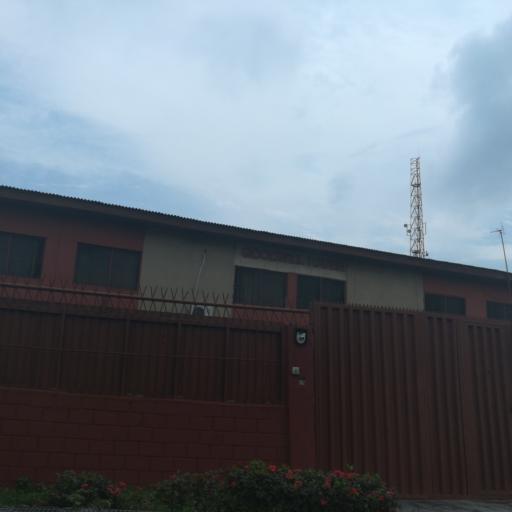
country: NG
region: Lagos
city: Ojota
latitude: 6.5750
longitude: 3.3953
